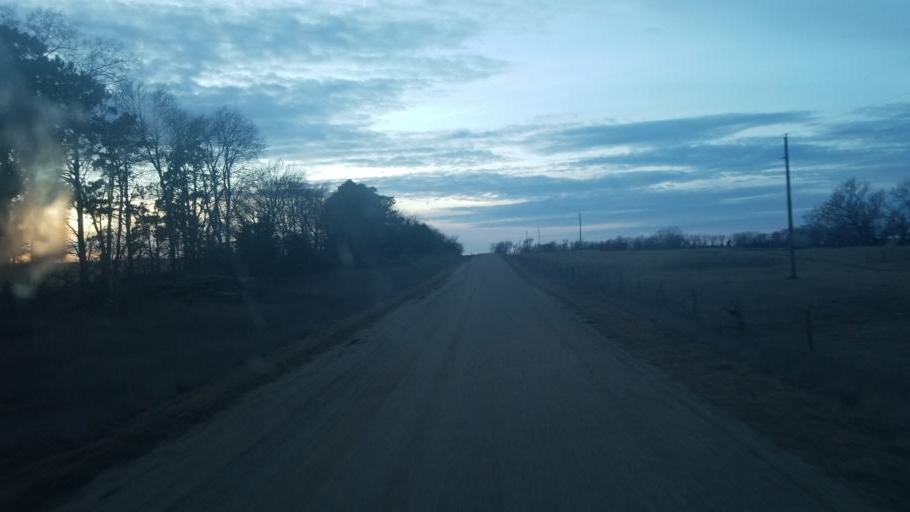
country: US
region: Nebraska
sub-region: Knox County
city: Center
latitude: 42.6554
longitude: -97.7745
